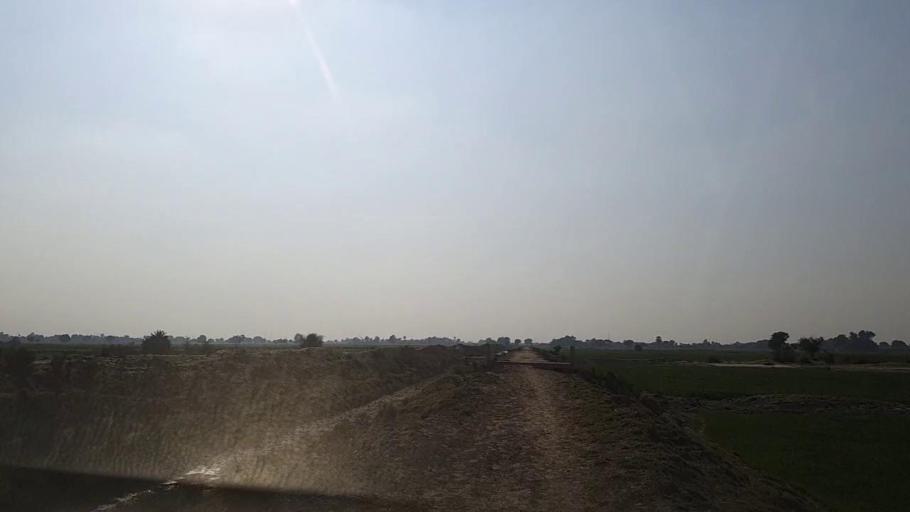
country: PK
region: Sindh
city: Moro
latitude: 26.7416
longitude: 67.9311
